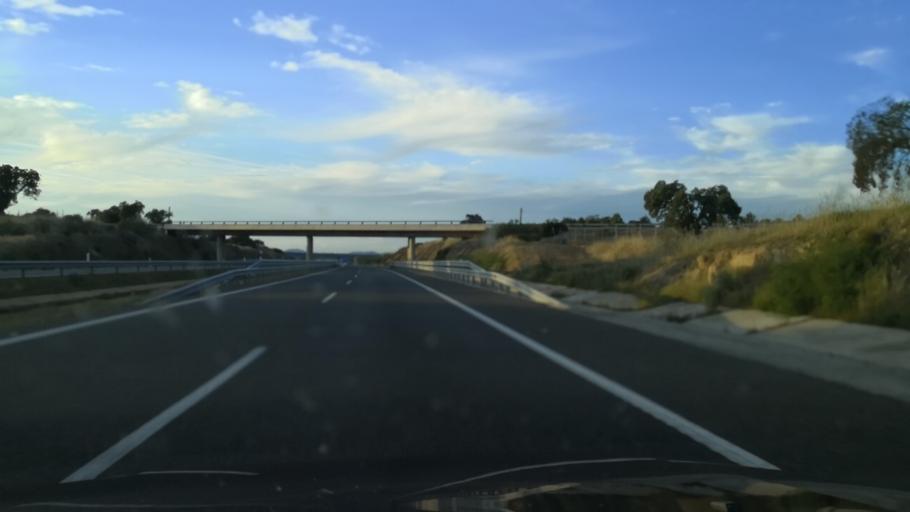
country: ES
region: Extremadura
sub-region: Provincia de Badajoz
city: Aljucen
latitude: 39.0185
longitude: -6.3305
